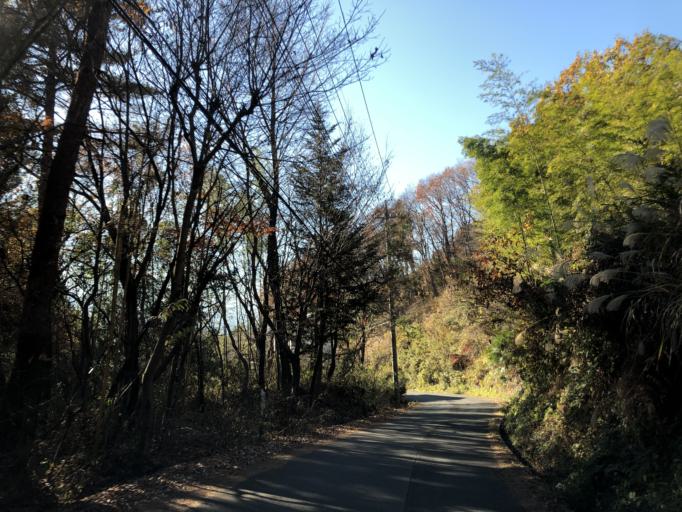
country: JP
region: Saitama
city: Chichibu
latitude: 35.9919
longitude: 139.1124
